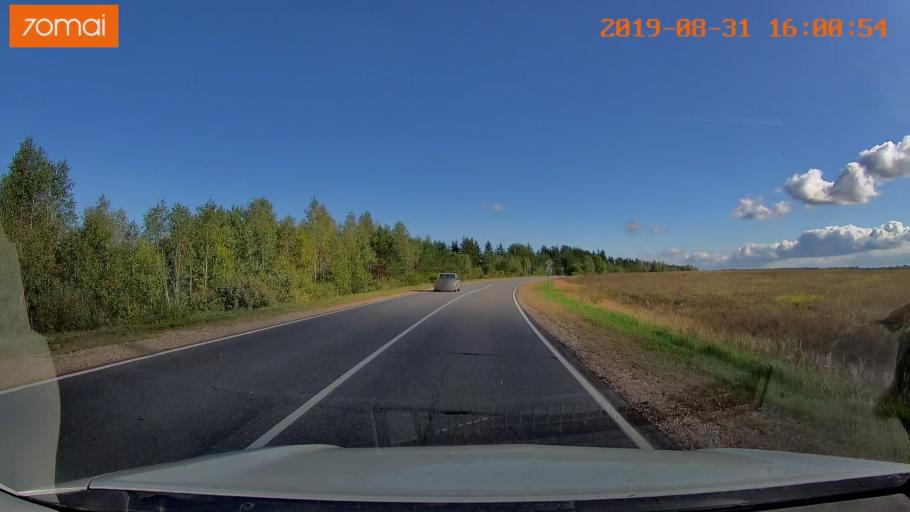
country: RU
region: Kaluga
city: Yukhnov
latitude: 54.6978
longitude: 35.2857
